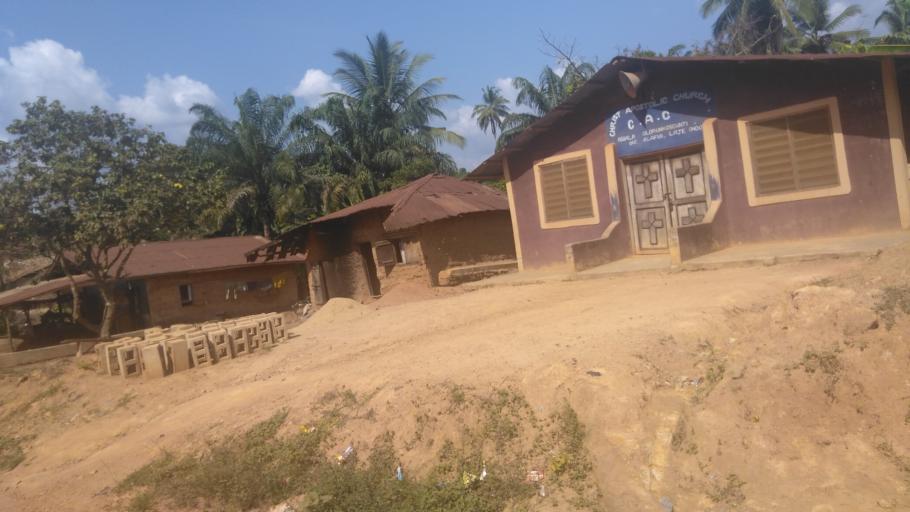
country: NG
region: Osun
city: Ifetedo
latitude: 7.0146
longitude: 4.6338
